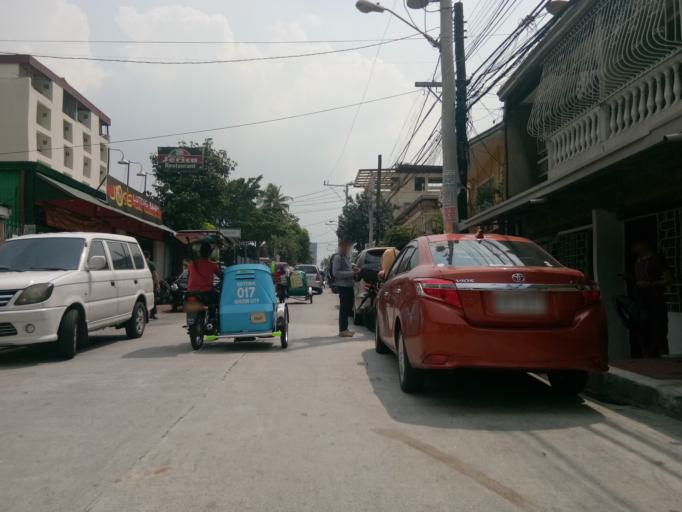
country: PH
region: Metro Manila
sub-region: San Juan
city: San Juan
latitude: 14.6170
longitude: 121.0568
